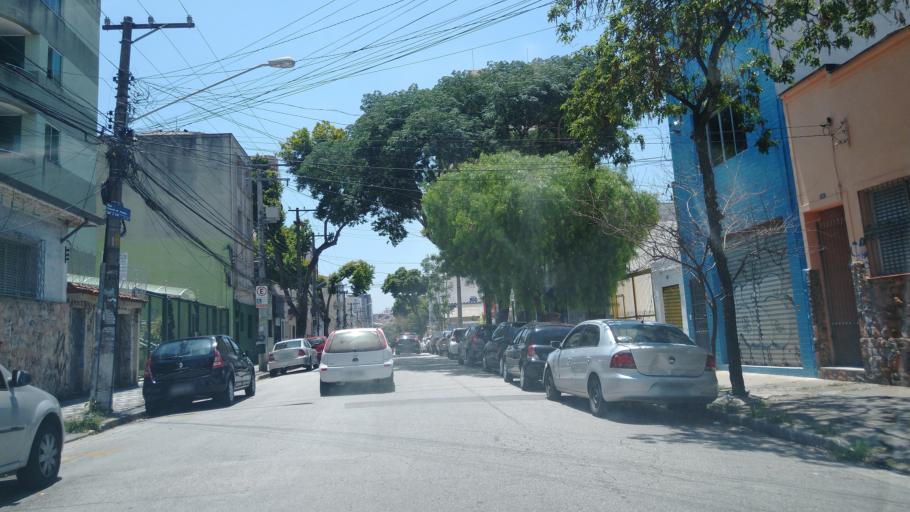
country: BR
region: Sao Paulo
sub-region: Sao Paulo
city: Sao Paulo
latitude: -23.5010
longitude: -46.6210
